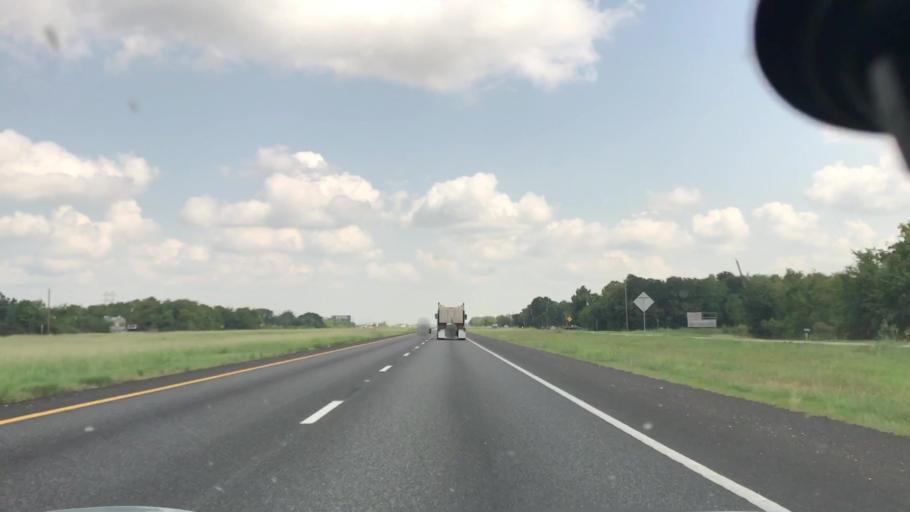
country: US
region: Texas
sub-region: Brazoria County
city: Rosharon
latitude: 29.3945
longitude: -95.4267
